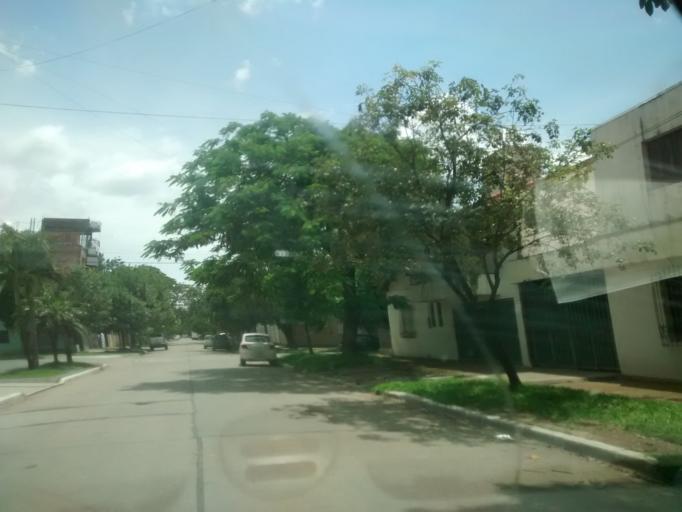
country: AR
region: Chaco
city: Resistencia
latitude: -27.4429
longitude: -58.9895
